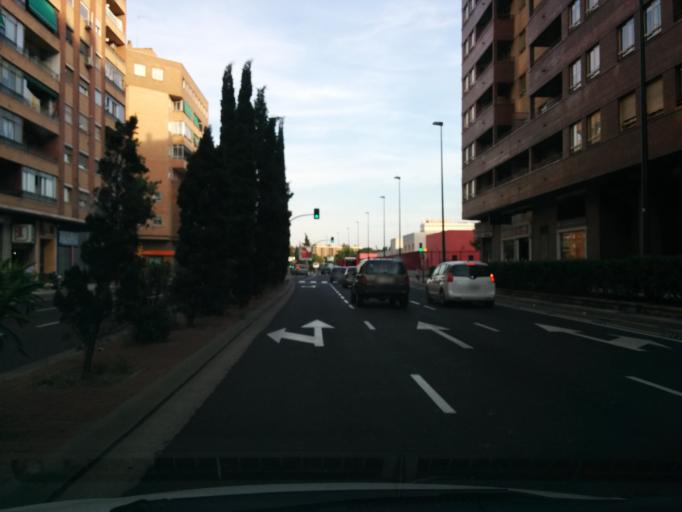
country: ES
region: Aragon
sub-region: Provincia de Zaragoza
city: Zaragoza
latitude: 41.6612
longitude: -0.8644
